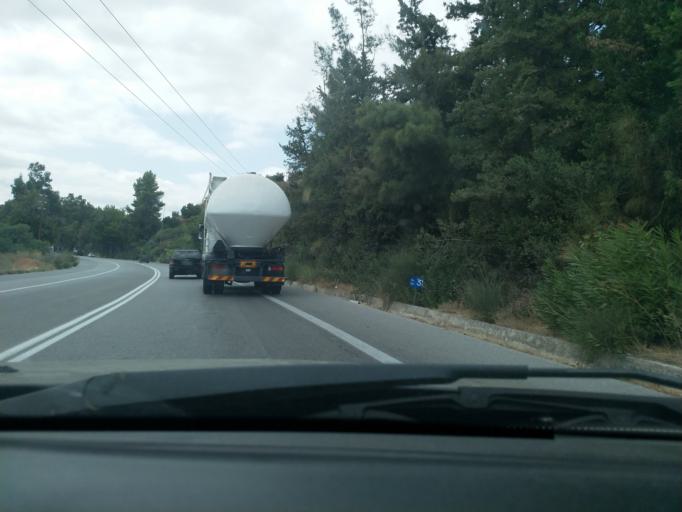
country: GR
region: Crete
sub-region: Nomos Chanias
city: Georgioupolis
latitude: 35.3781
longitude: 24.2060
